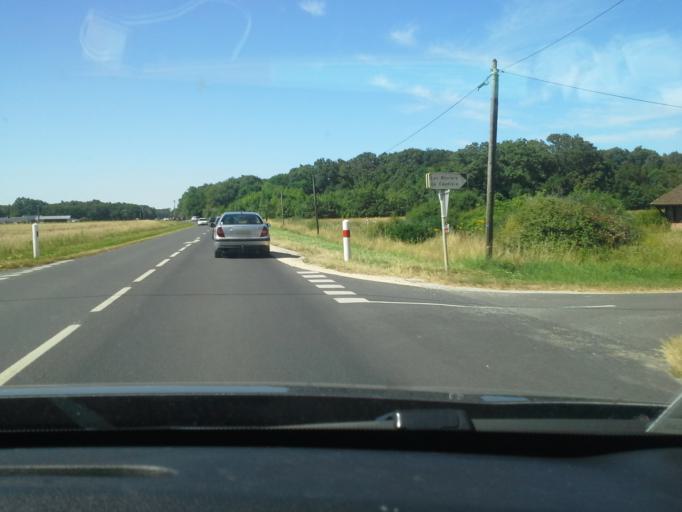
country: FR
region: Centre
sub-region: Departement du Loir-et-Cher
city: Cormeray
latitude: 47.5034
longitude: 1.4051
